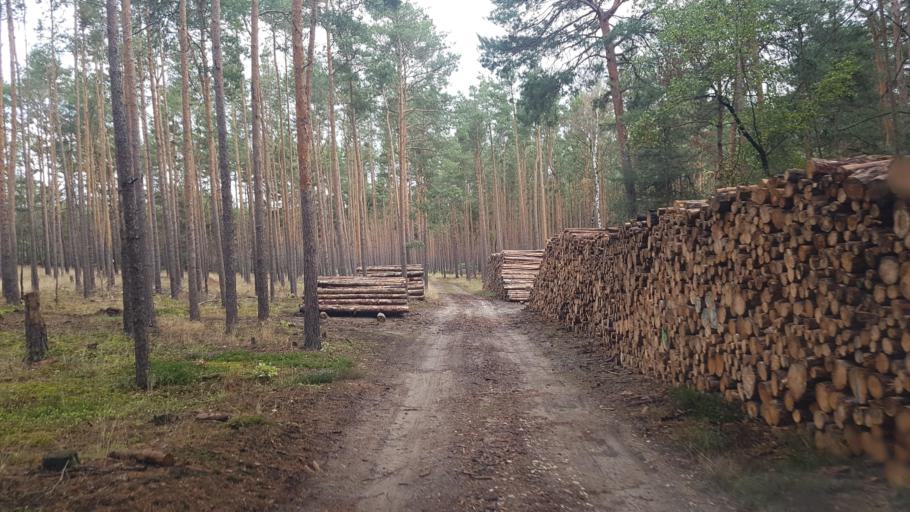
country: DE
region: Brandenburg
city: Elsterwerda
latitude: 51.4872
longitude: 13.4617
